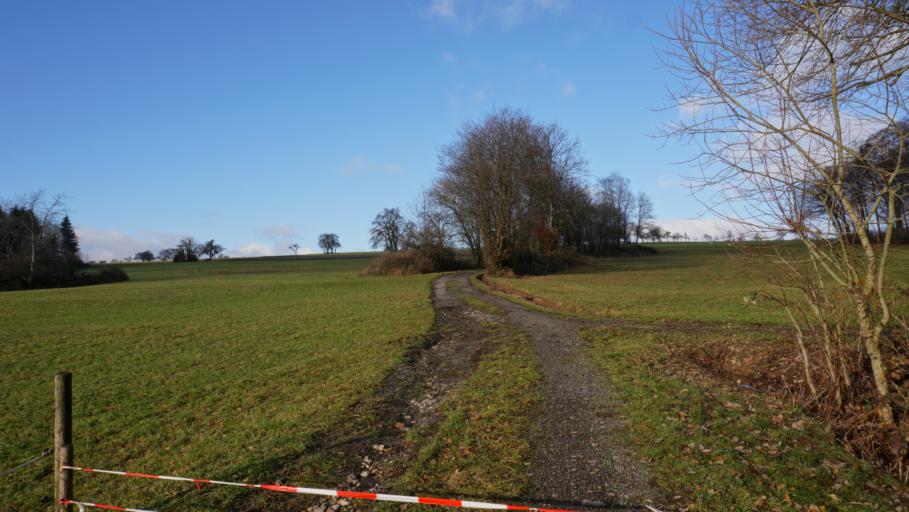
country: DE
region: Baden-Wuerttemberg
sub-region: Karlsruhe Region
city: Fahrenbach
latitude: 49.4361
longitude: 9.1117
